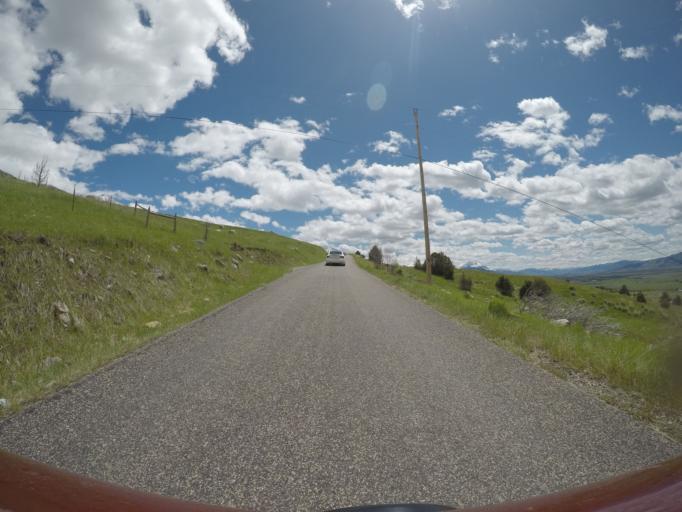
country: US
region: Montana
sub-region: Park County
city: Livingston
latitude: 45.5004
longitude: -110.5563
